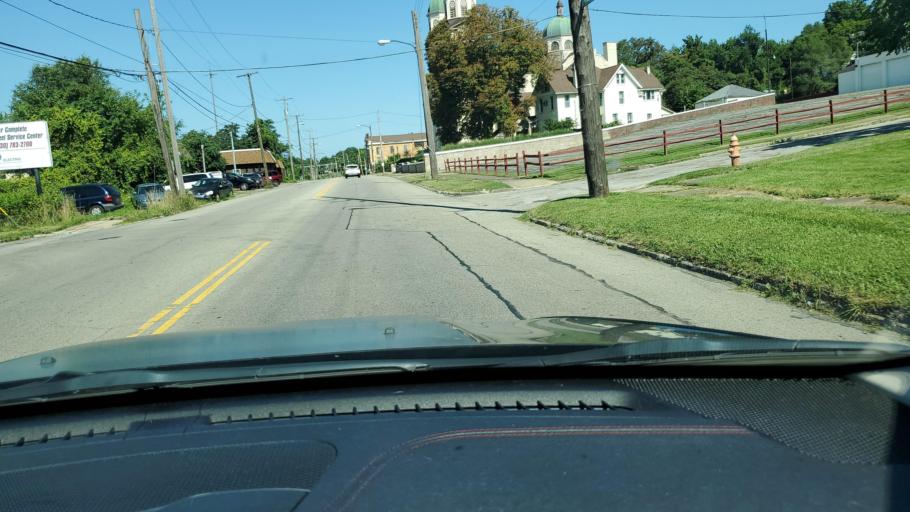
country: US
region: Ohio
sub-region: Mahoning County
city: Campbell
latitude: 41.0825
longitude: -80.6153
